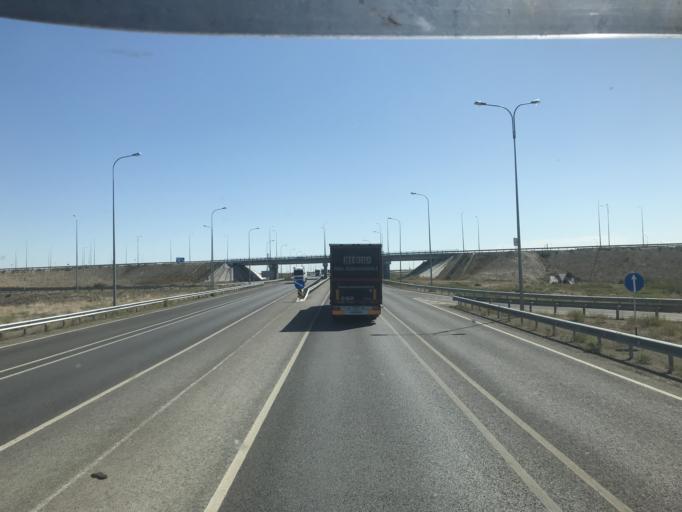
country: KZ
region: Qyzylorda
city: Dzhalagash
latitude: 44.9919
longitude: 64.5238
